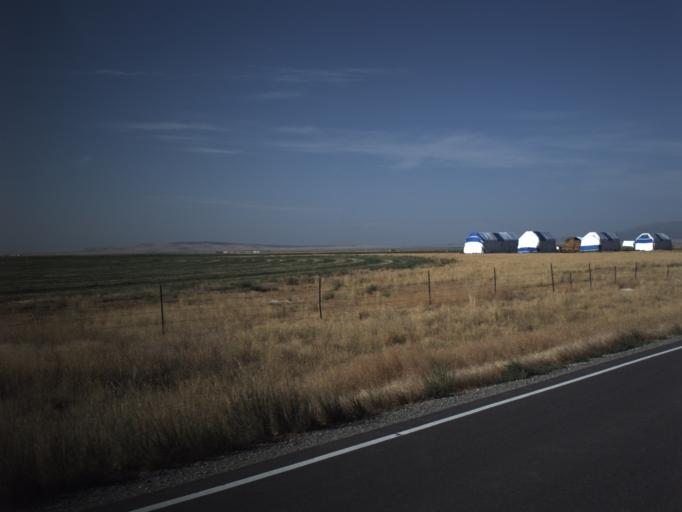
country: US
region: Idaho
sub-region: Oneida County
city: Malad City
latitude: 41.9670
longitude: -112.8690
